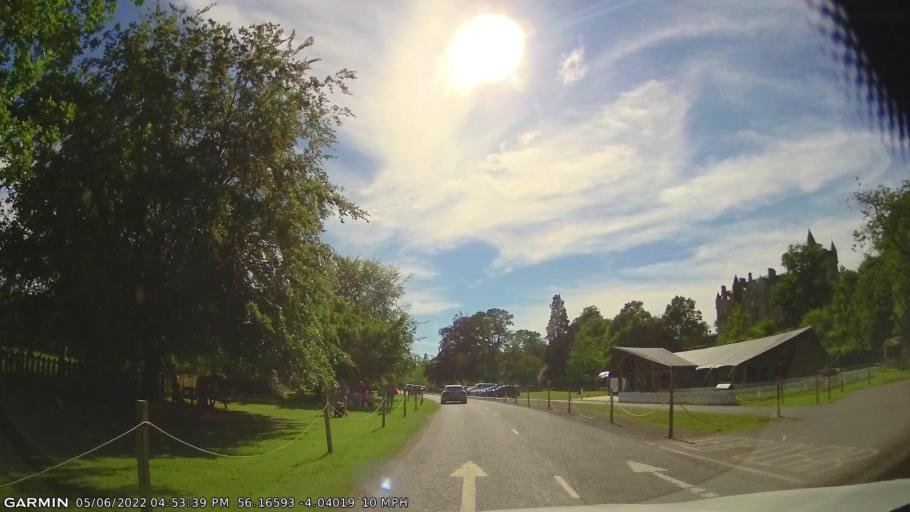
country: GB
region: Scotland
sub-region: Stirling
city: Doune
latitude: 56.1654
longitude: -4.0420
